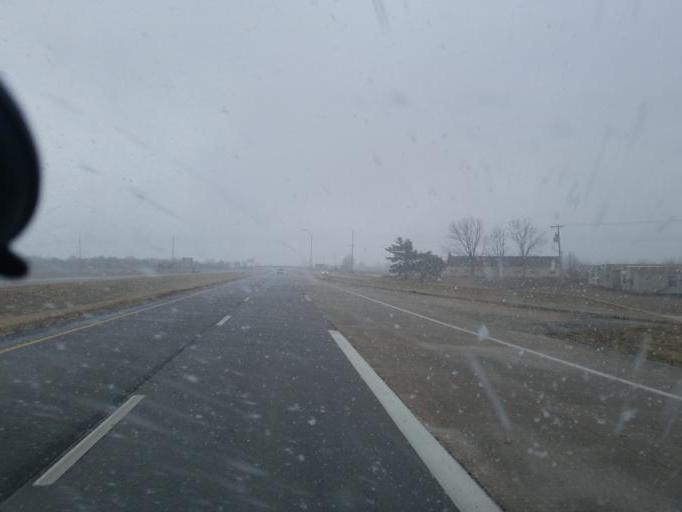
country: US
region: Missouri
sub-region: Randolph County
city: Moberly
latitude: 39.4407
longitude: -92.4221
